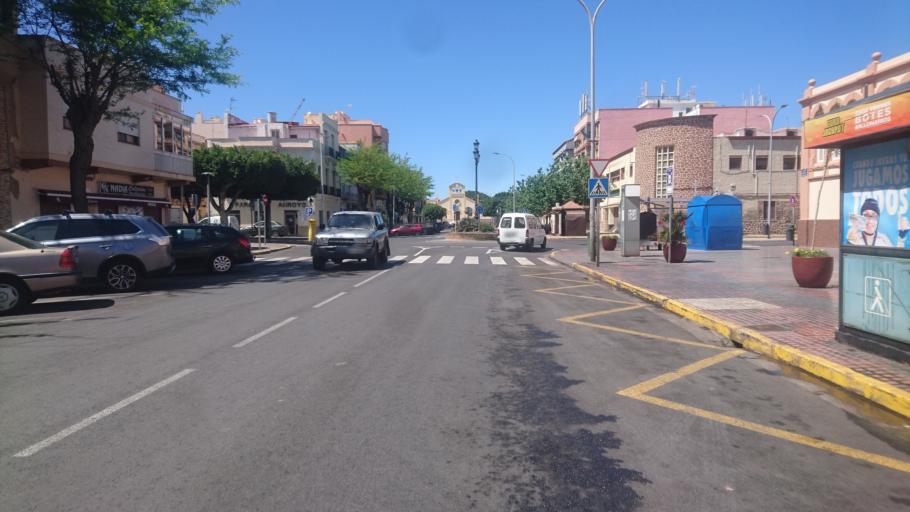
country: ES
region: Melilla
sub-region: Melilla
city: Melilla
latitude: 35.2767
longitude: -2.9394
